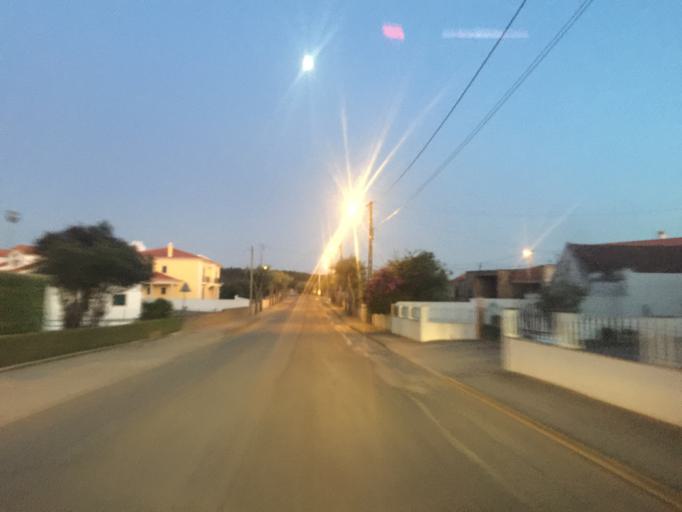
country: PT
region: Lisbon
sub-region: Lourinha
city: Lourinha
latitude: 39.2742
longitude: -9.2766
